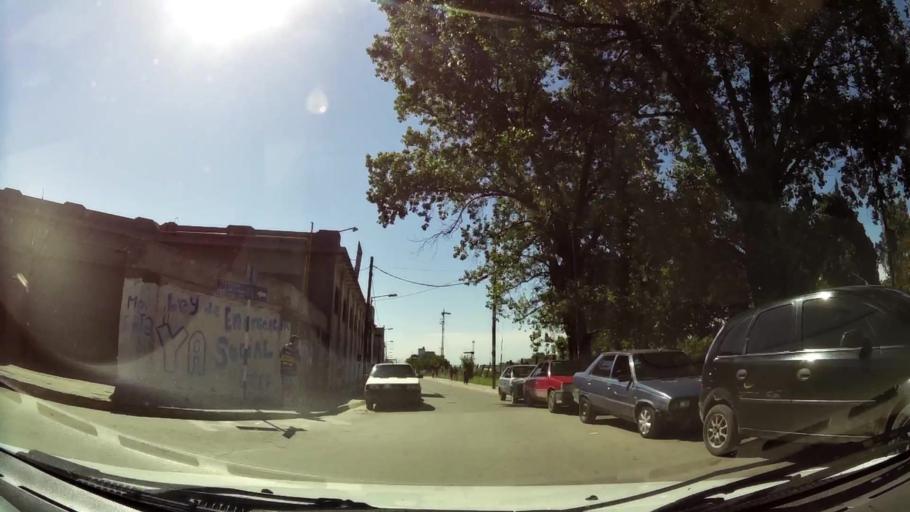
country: AR
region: Buenos Aires
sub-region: Partido de General San Martin
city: General San Martin
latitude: -34.5343
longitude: -58.5771
